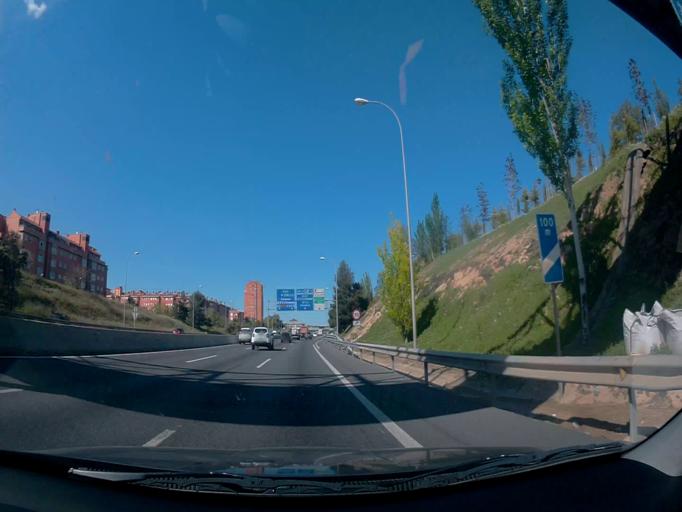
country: ES
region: Madrid
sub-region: Provincia de Madrid
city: Vicalvaro
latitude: 40.4019
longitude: -3.6259
